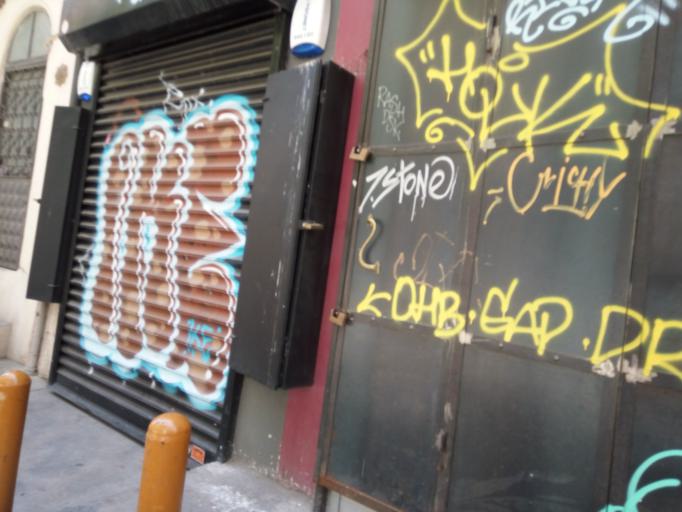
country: TR
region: Istanbul
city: Eminoenue
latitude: 41.0332
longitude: 28.9817
